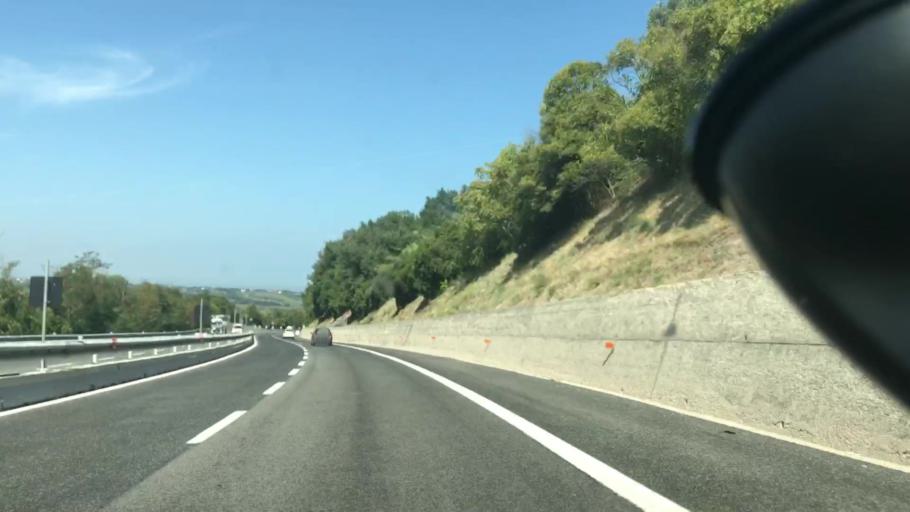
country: IT
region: Abruzzo
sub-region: Provincia di Chieti
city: Vasto
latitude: 42.1408
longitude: 14.6595
